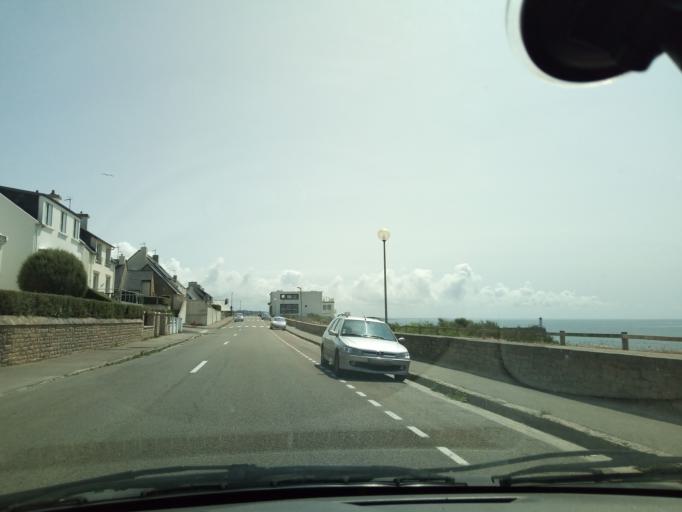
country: FR
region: Brittany
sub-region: Departement du Finistere
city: Audierne
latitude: 48.0123
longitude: -4.5453
